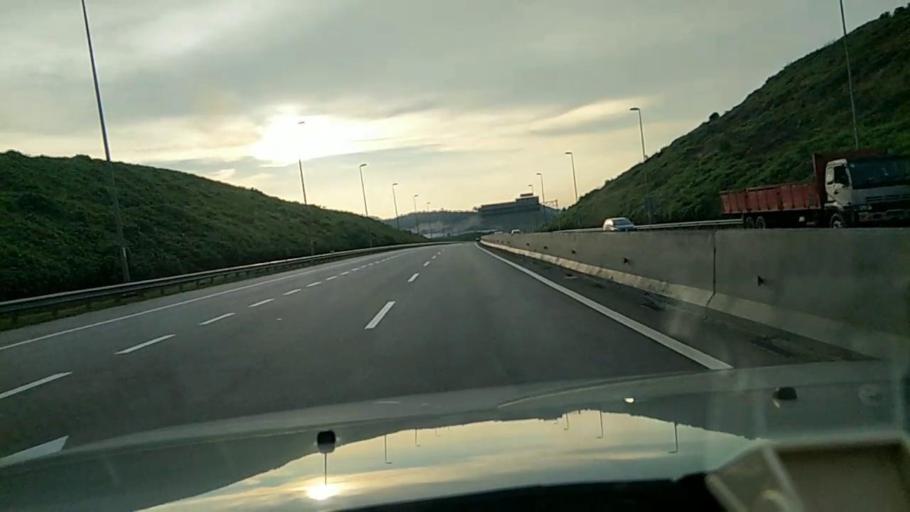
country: MY
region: Selangor
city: Batu Arang
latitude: 3.2734
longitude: 101.4592
